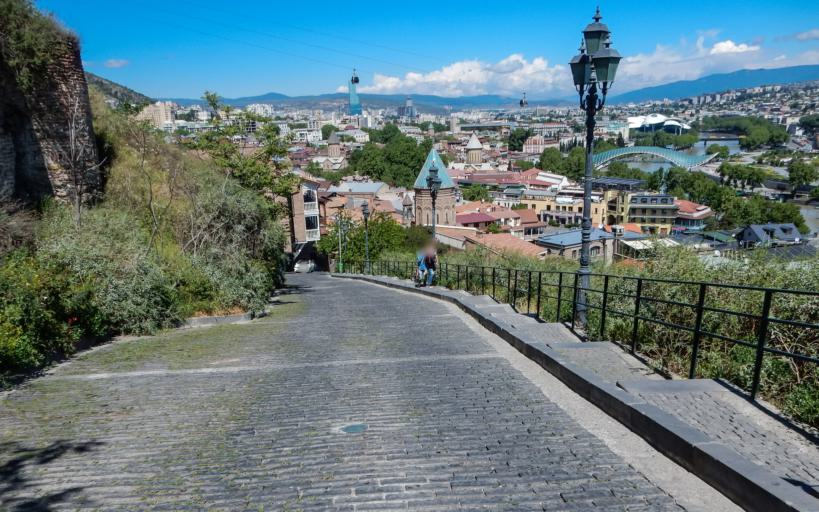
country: GE
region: T'bilisi
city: Tbilisi
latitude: 41.6881
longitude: 44.8097
